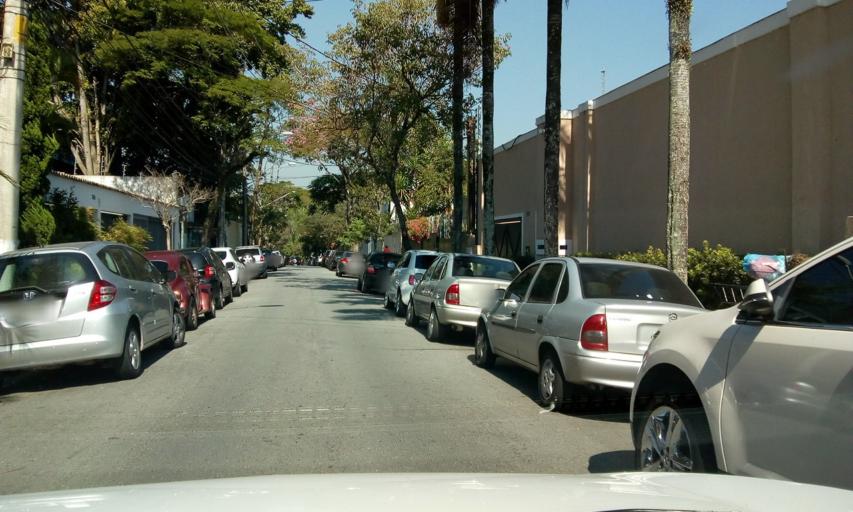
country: BR
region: Sao Paulo
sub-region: Taboao Da Serra
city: Taboao da Serra
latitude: -23.5966
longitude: -46.7095
